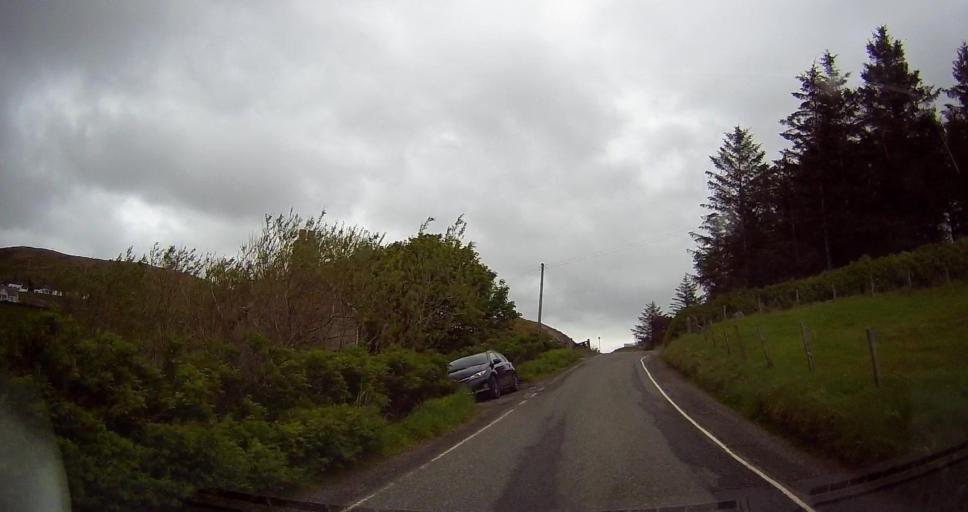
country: GB
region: Scotland
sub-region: Shetland Islands
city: Lerwick
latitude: 60.3505
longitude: -1.2636
